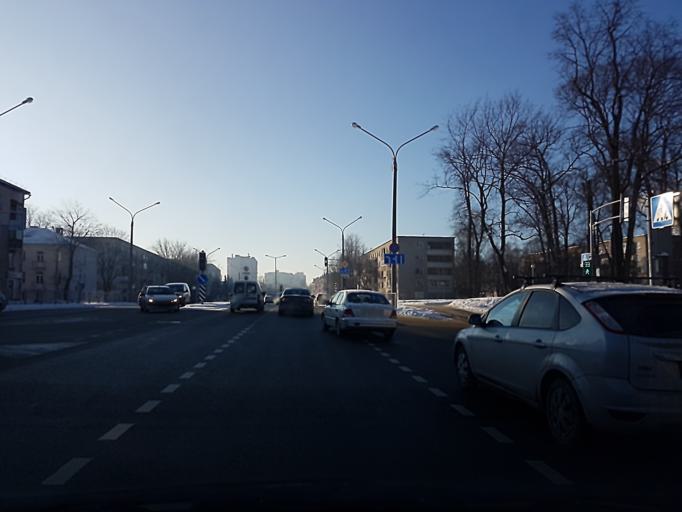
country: BY
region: Minsk
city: Minsk
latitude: 53.8965
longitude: 27.5281
